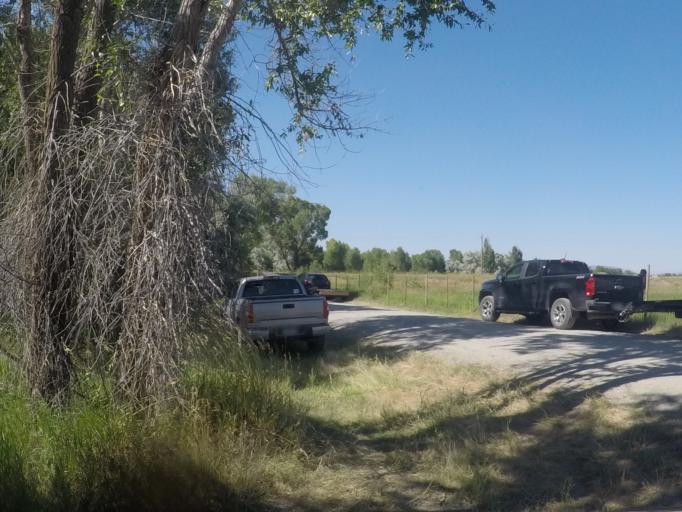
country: US
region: Montana
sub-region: Park County
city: Livingston
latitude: 45.3670
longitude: -110.7254
